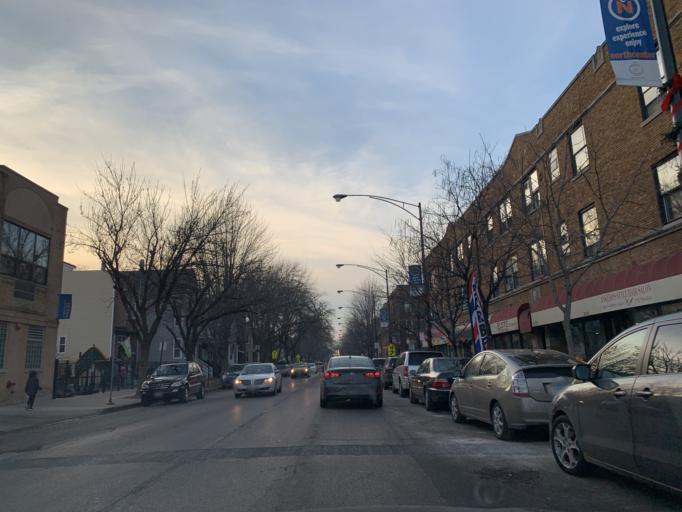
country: US
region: Illinois
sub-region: Cook County
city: Lincolnwood
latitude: 41.9615
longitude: -87.6799
